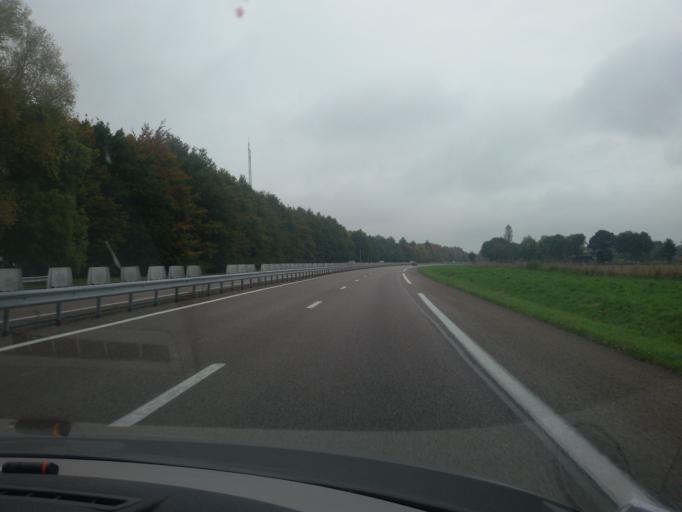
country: FR
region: Haute-Normandie
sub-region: Departement de l'Eure
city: Manneville-sur-Risle
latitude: 49.3944
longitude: 0.5395
